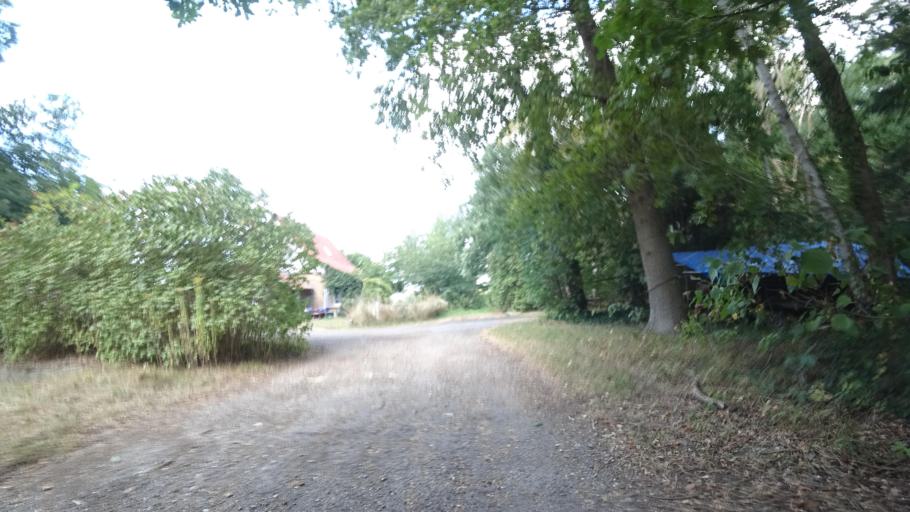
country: DE
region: North Rhine-Westphalia
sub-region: Regierungsbezirk Detmold
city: Verl
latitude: 51.9392
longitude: 8.4999
